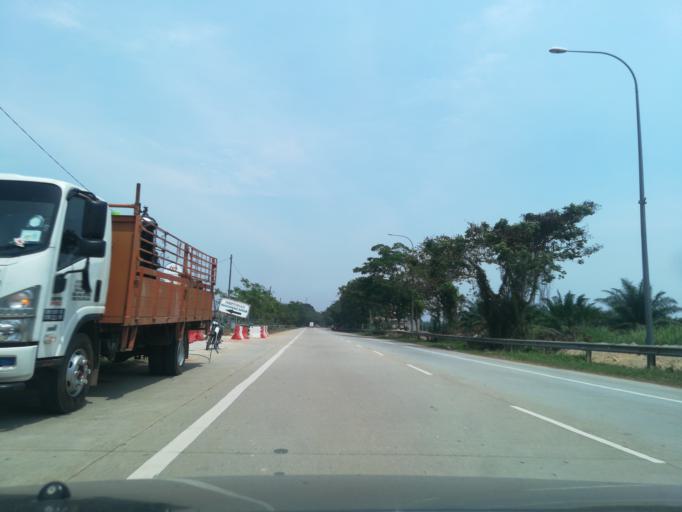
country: MY
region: Kedah
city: Kulim
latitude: 5.4280
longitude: 100.5611
